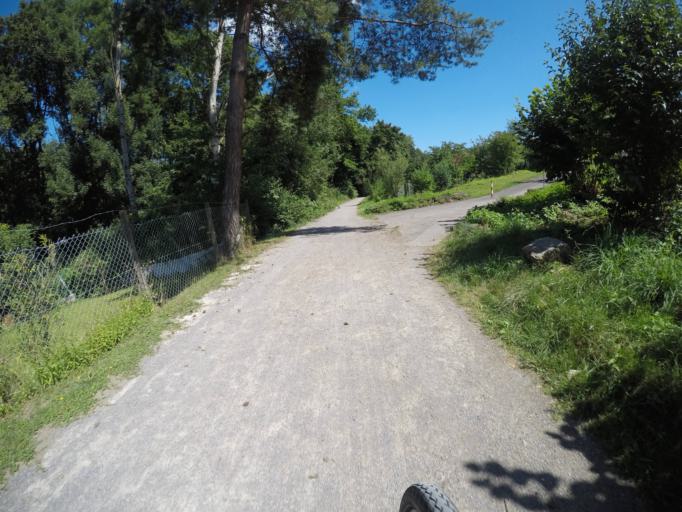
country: DE
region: Baden-Wuerttemberg
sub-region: Regierungsbezirk Stuttgart
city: Leinfelden-Echterdingen
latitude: 48.7164
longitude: 9.1639
